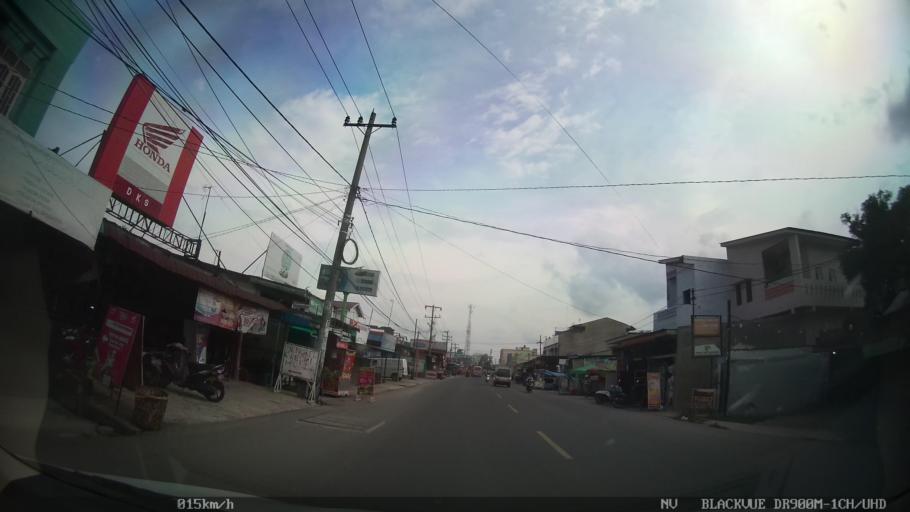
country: ID
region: North Sumatra
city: Medan
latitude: 3.6033
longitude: 98.7577
